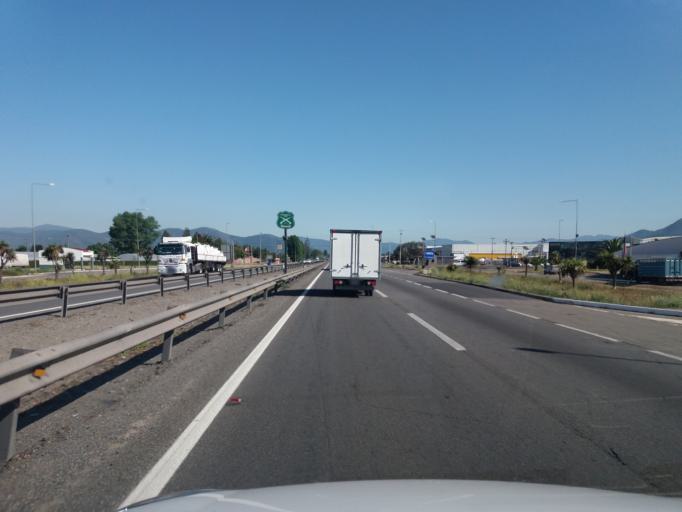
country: CL
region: Valparaiso
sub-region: Provincia de Quillota
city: Hacienda La Calera
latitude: -32.8019
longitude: -71.1550
